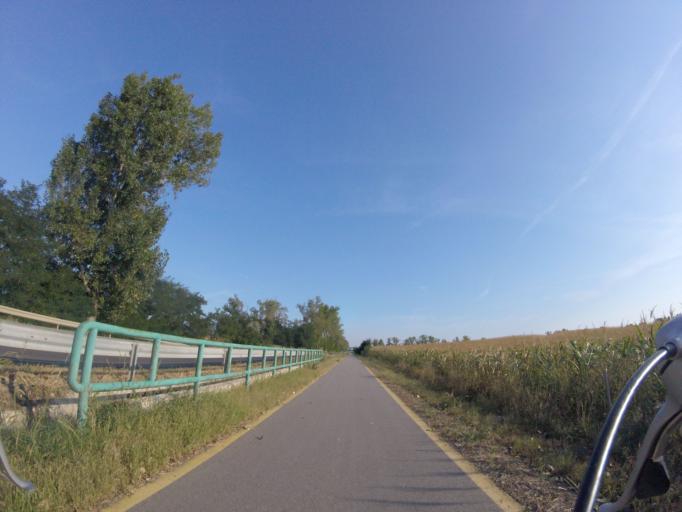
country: HU
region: Szabolcs-Szatmar-Bereg
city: Tiszanagyfalu
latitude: 48.0934
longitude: 21.4944
